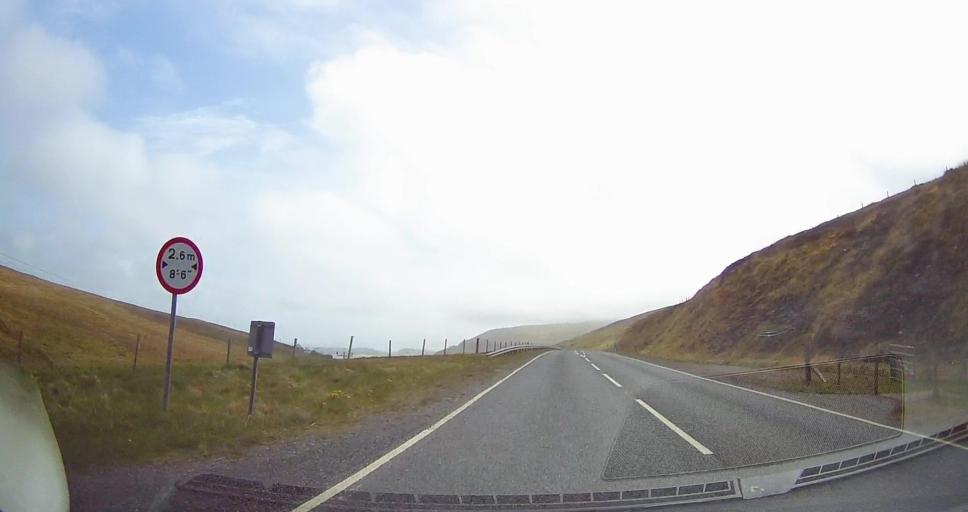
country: GB
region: Scotland
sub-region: Shetland Islands
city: Sandwick
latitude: 60.0016
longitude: -1.2794
